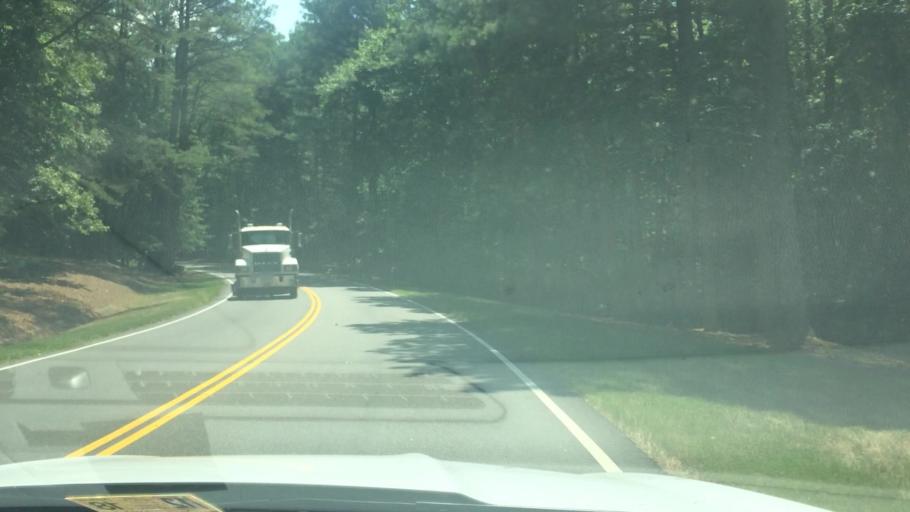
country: US
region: Virginia
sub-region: City of Williamsburg
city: Williamsburg
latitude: 37.2410
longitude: -76.6608
